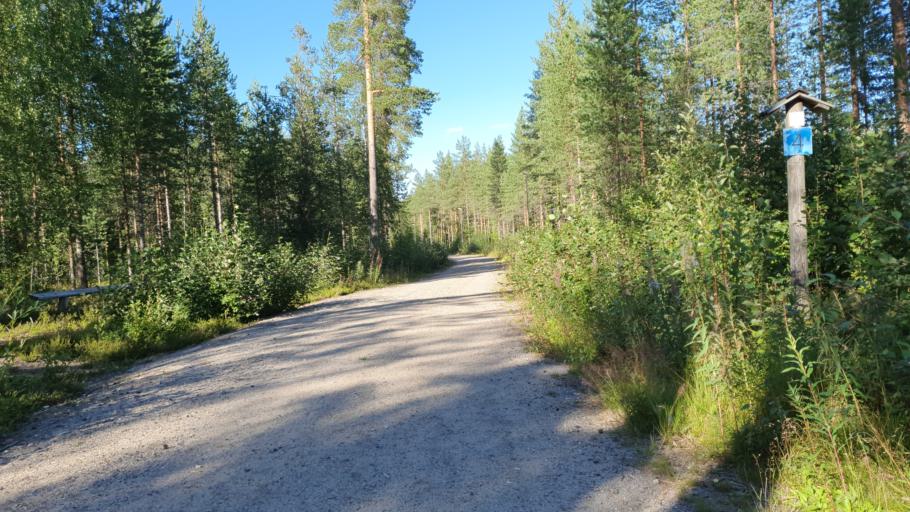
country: FI
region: Kainuu
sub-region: Kehys-Kainuu
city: Kuhmo
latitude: 64.1109
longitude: 29.5133
